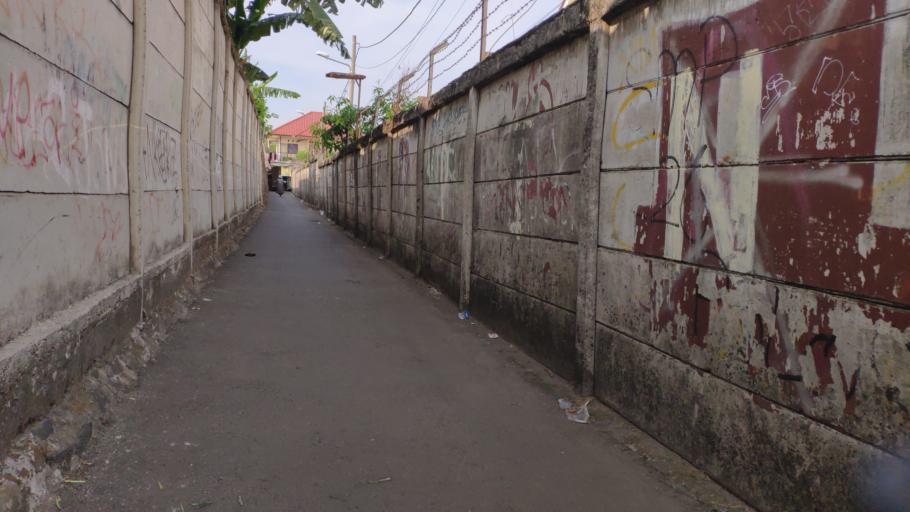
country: ID
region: West Java
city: Pamulang
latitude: -6.3123
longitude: 106.7976
